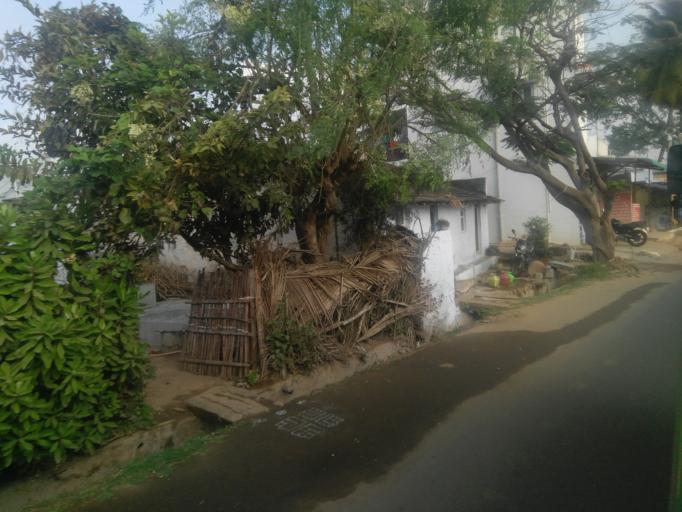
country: IN
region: Tamil Nadu
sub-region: Coimbatore
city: Perur
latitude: 11.0368
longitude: 76.8911
